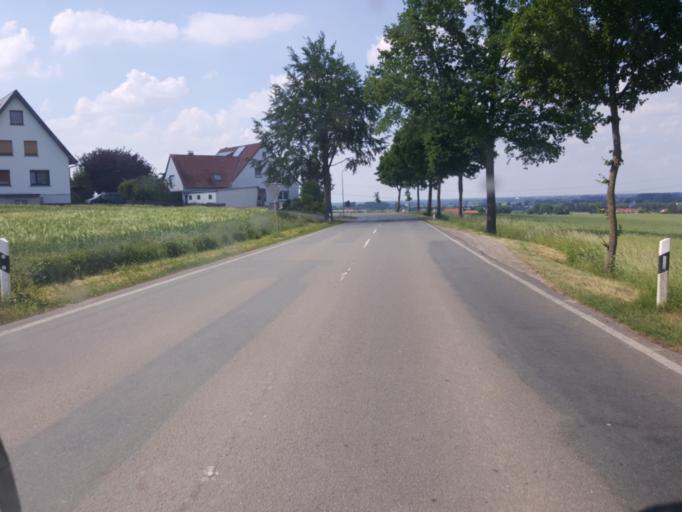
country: DE
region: North Rhine-Westphalia
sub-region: Regierungsbezirk Detmold
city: Hille
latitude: 52.2747
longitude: 8.7746
